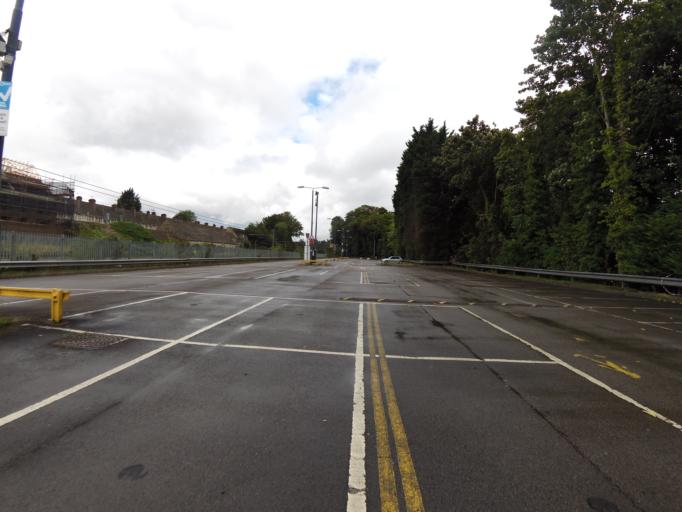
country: GB
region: England
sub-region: Hertfordshire
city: Radlett
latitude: 51.6870
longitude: -0.3178
